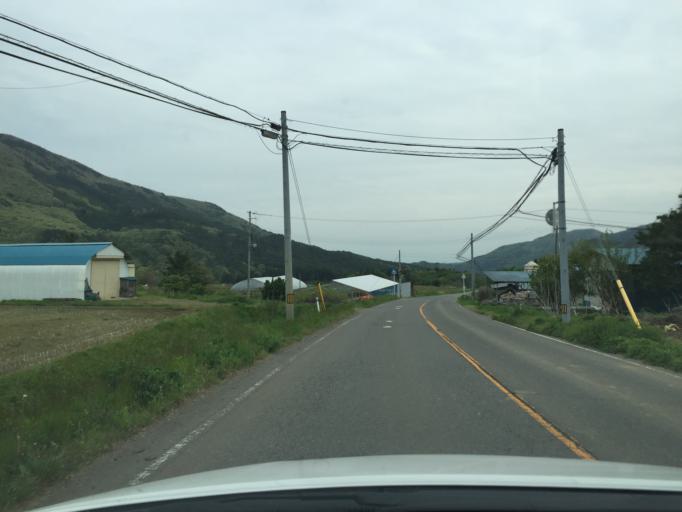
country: JP
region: Fukushima
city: Motomiya
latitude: 37.5335
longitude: 140.2660
